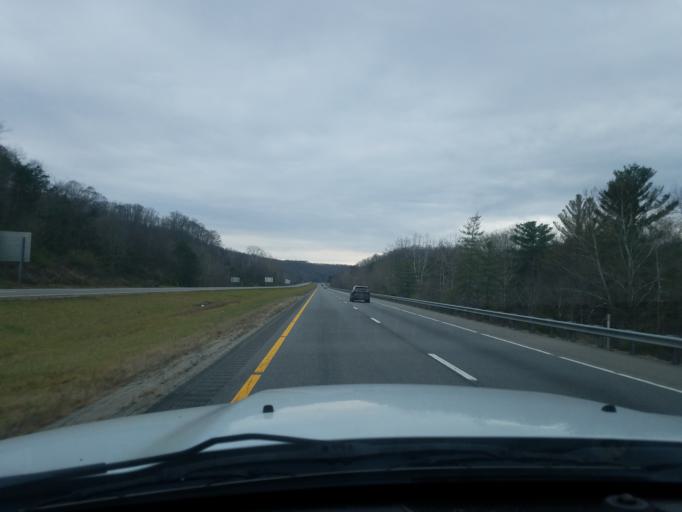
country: US
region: Kentucky
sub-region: Boyd County
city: Meads
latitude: 38.3642
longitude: -82.7187
